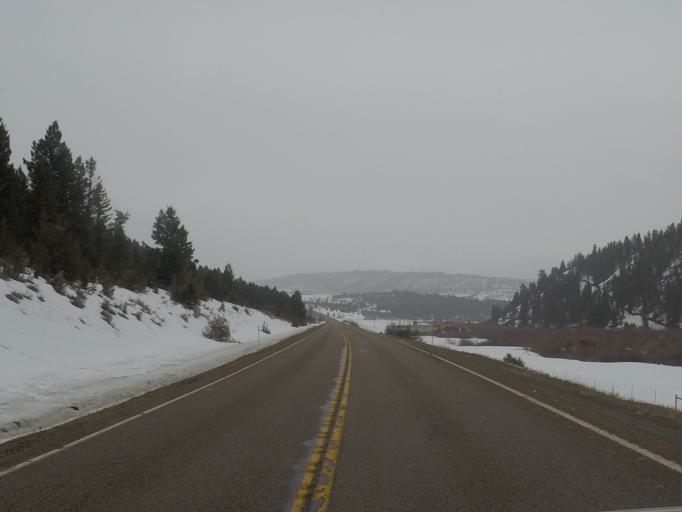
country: US
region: Montana
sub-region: Meagher County
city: White Sulphur Springs
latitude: 46.6768
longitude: -110.8781
